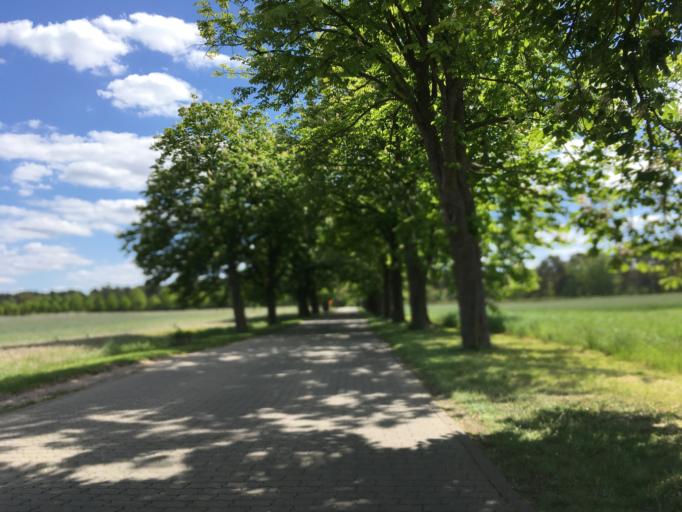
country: DE
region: Brandenburg
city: Biesenthal
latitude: 52.7512
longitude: 13.6475
